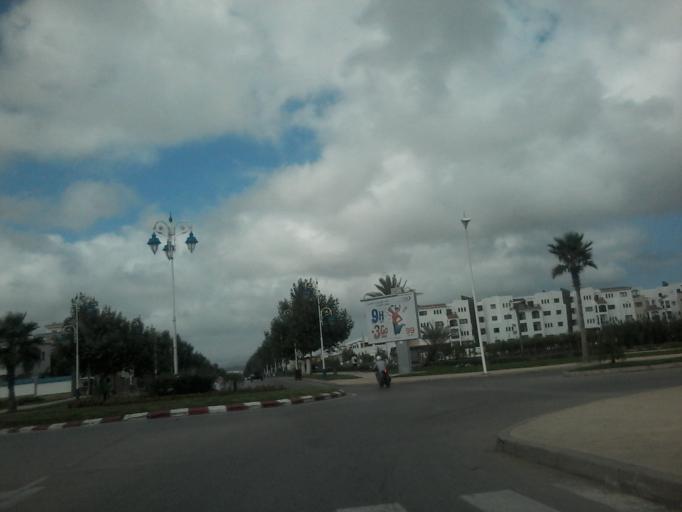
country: MA
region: Tanger-Tetouan
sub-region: Tetouan
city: Martil
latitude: 35.6310
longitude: -5.2846
